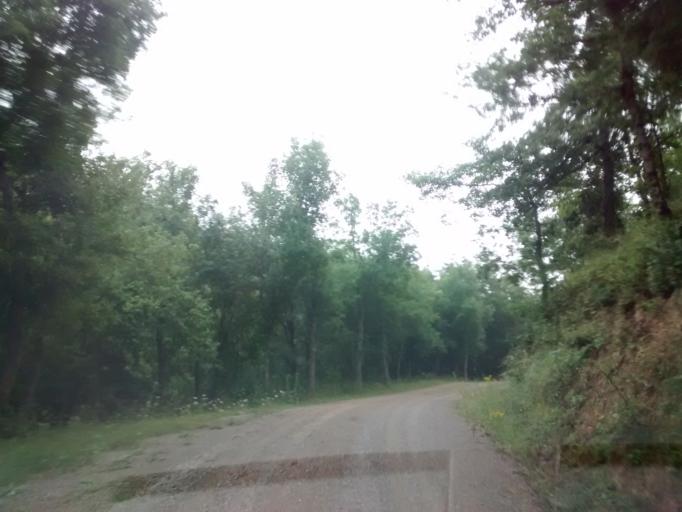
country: ES
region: La Rioja
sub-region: Provincia de La Rioja
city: Ajamil
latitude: 42.1436
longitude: -2.4783
